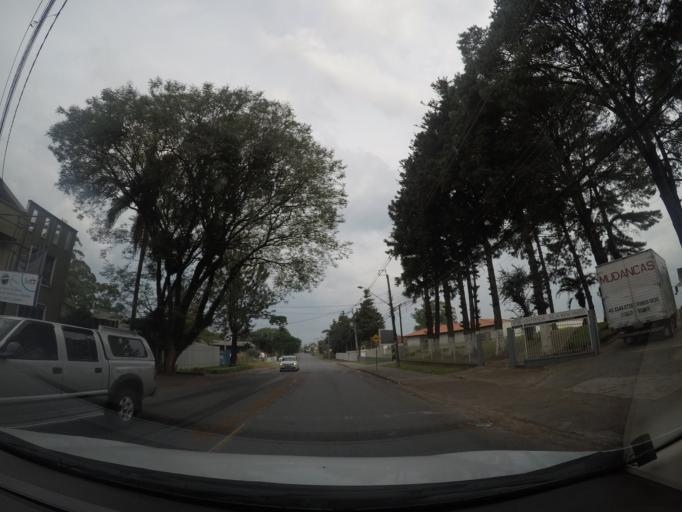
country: BR
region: Parana
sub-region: Sao Jose Dos Pinhais
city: Sao Jose dos Pinhais
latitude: -25.5139
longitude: -49.2607
